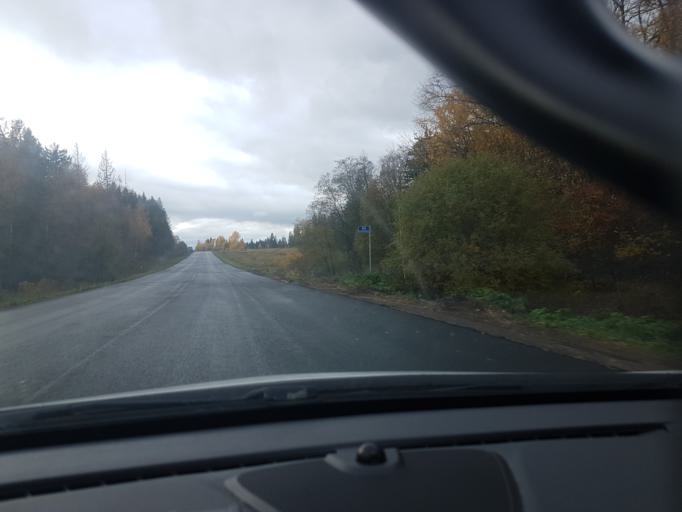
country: RU
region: Moskovskaya
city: Sychevo
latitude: 56.0042
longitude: 36.3054
